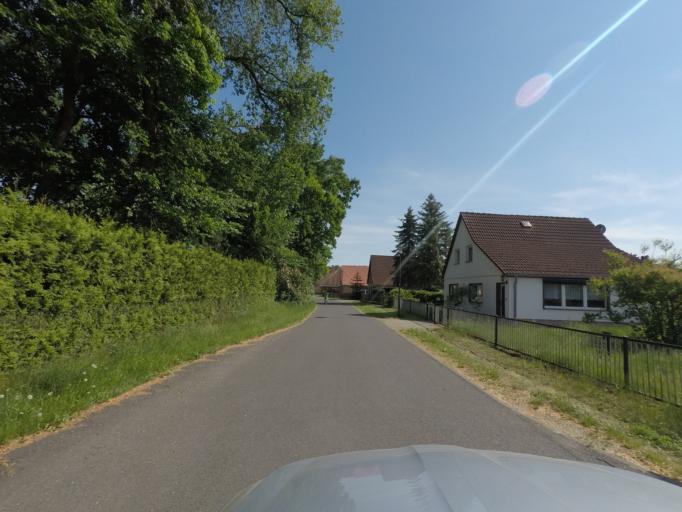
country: DE
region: Brandenburg
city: Melchow
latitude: 52.8627
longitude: 13.7189
